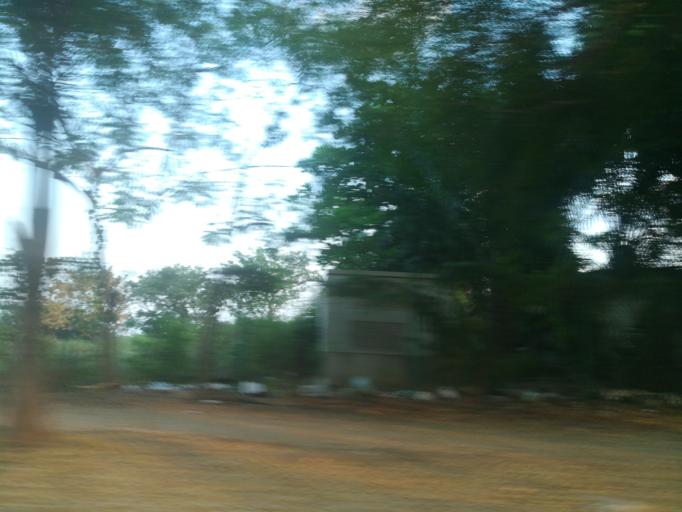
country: NG
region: Abuja Federal Capital Territory
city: Abuja
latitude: 9.0707
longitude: 7.4146
